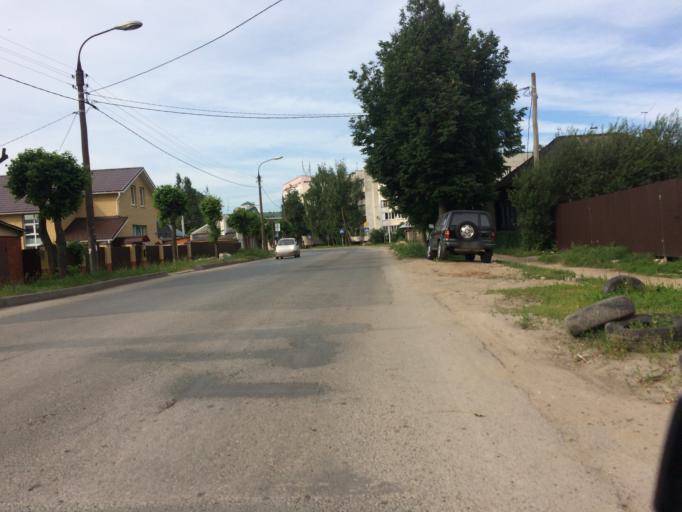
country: RU
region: Mariy-El
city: Yoshkar-Ola
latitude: 56.6459
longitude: 47.9056
